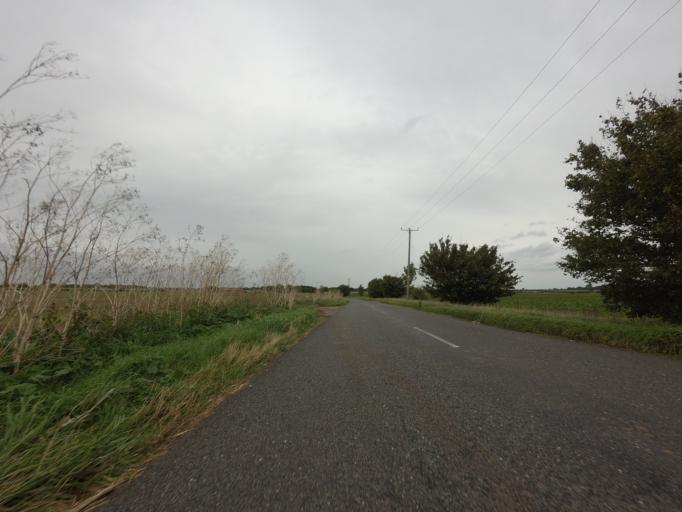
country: GB
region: England
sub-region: Cambridgeshire
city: Harston
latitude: 52.0789
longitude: 0.0846
